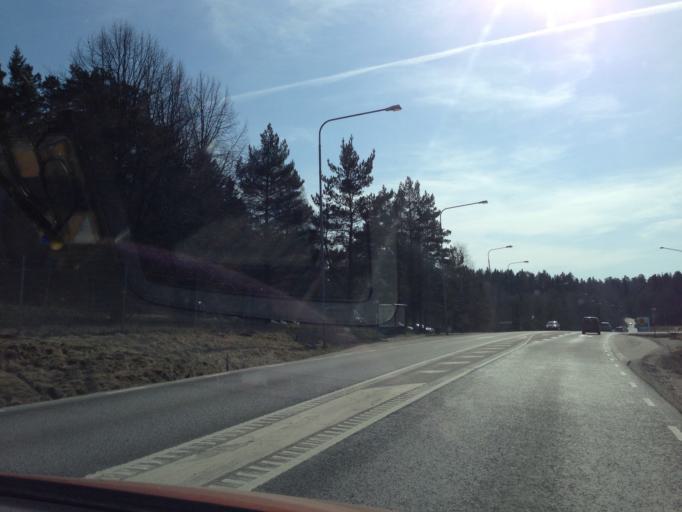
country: SE
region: Stockholm
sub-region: Salems Kommun
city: Ronninge
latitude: 59.2119
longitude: 17.7550
